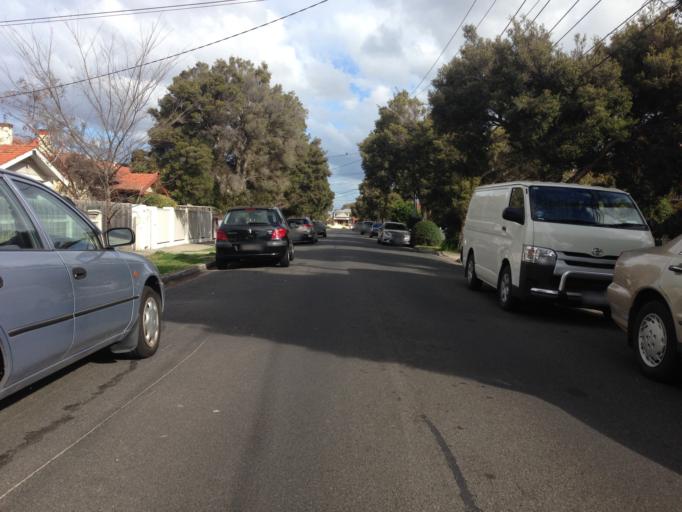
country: AU
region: Victoria
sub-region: Darebin
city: Northcote
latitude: -37.7714
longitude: 145.0079
